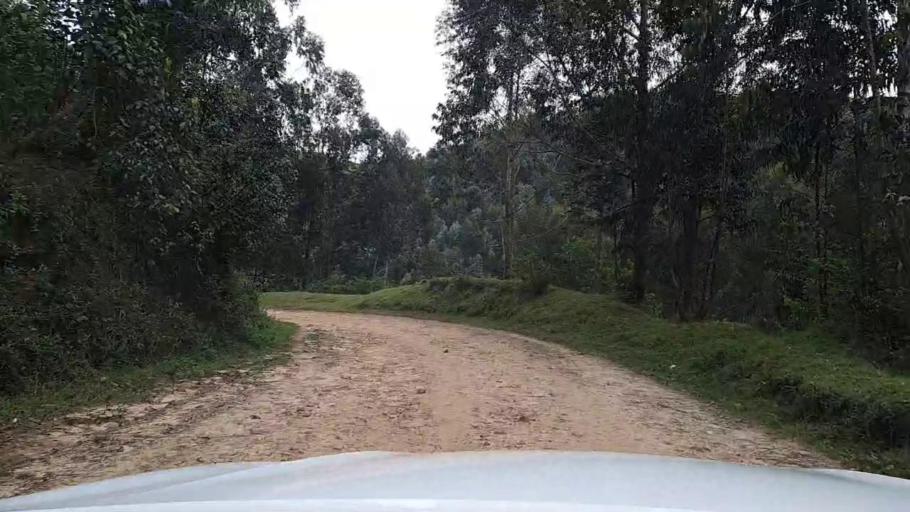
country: RW
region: Western Province
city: Kibuye
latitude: -2.2729
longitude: 29.3643
